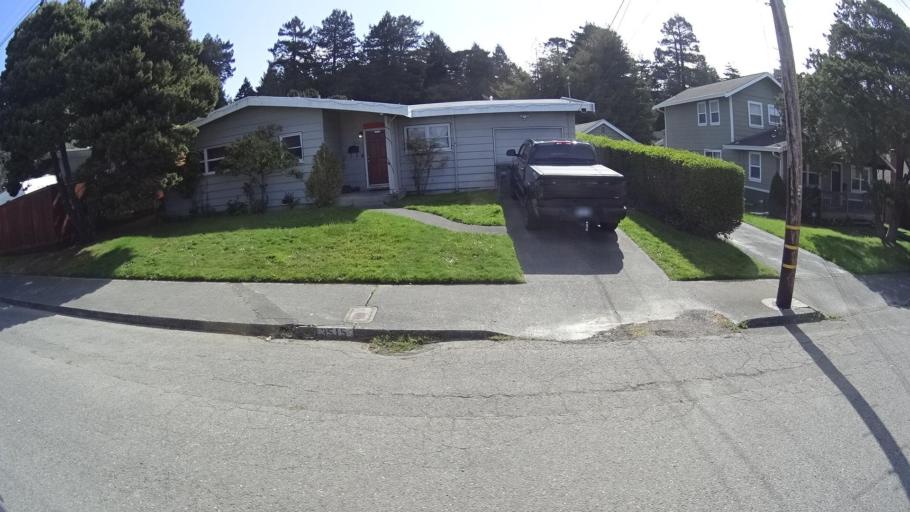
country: US
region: California
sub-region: Humboldt County
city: Cutten
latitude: 40.7756
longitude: -124.1602
